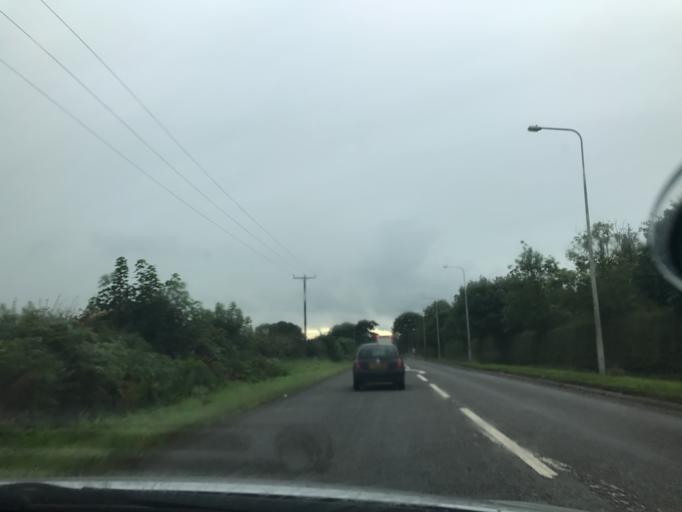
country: GB
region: England
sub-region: Cheshire West and Chester
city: Oakmere
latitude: 53.2265
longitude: -2.6241
